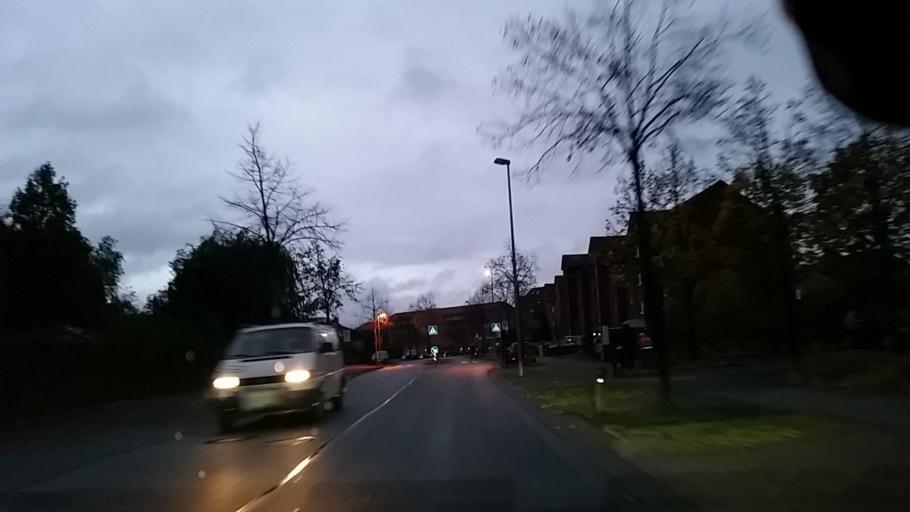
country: DE
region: Lower Saxony
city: Wolfsburg
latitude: 52.4151
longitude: 10.8332
